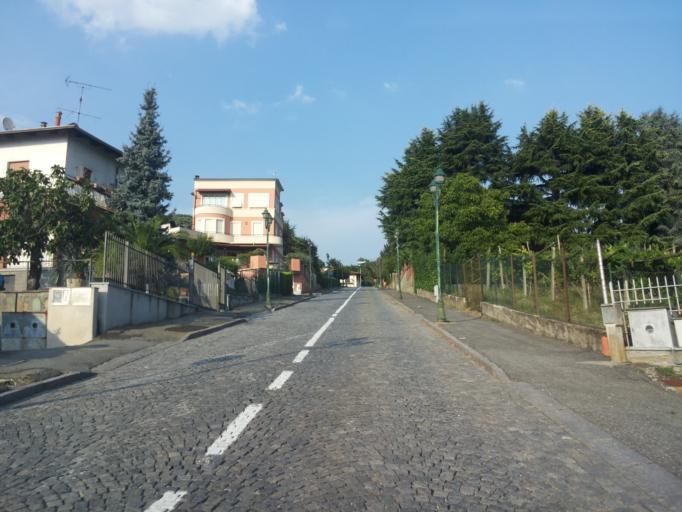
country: IT
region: Piedmont
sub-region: Provincia di Biella
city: Viverone
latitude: 45.4219
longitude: 8.0499
